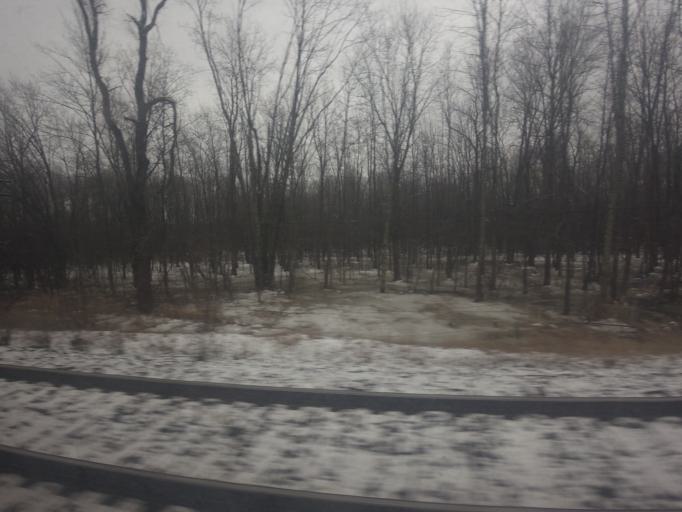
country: CA
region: Ontario
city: Belleville
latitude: 44.1541
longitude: -77.4664
